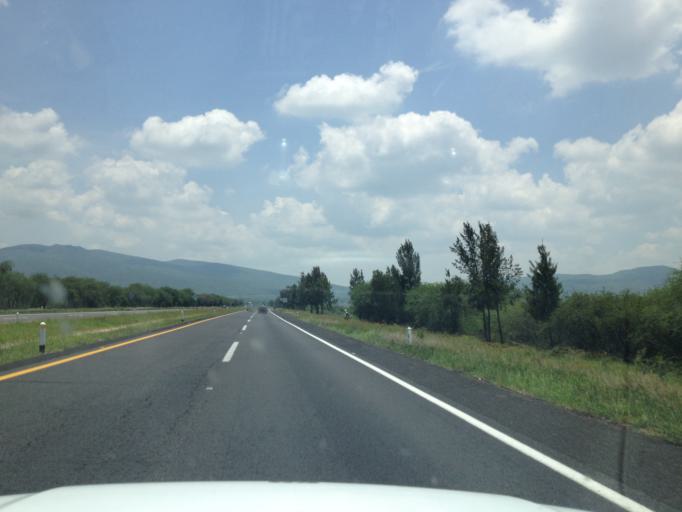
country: MX
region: Michoacan
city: Ecuandureo
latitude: 20.1799
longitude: -102.2697
